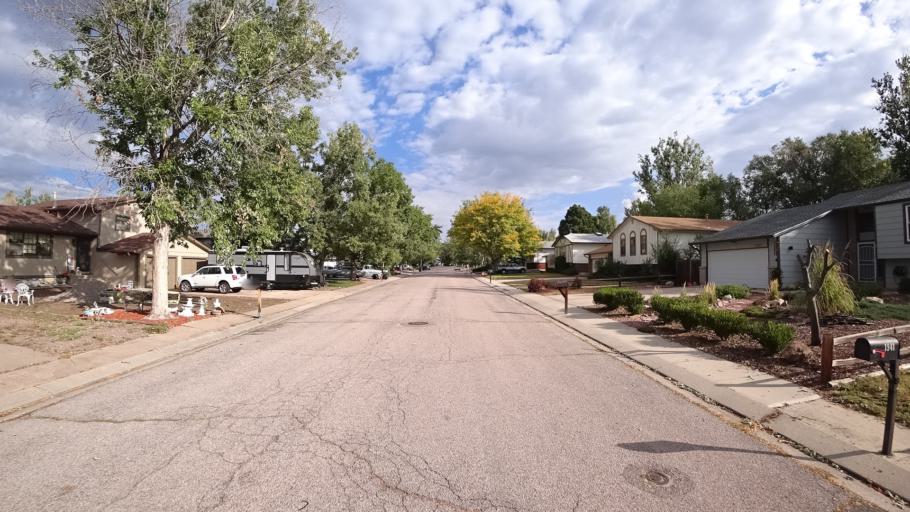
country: US
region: Colorado
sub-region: El Paso County
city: Cimarron Hills
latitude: 38.8583
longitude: -104.7513
